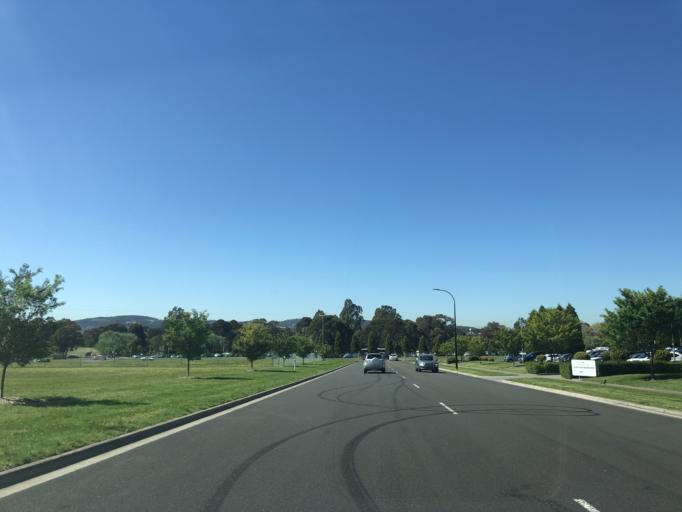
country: AU
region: Victoria
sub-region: Knox
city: Scoresby
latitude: -37.9045
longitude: 145.2247
